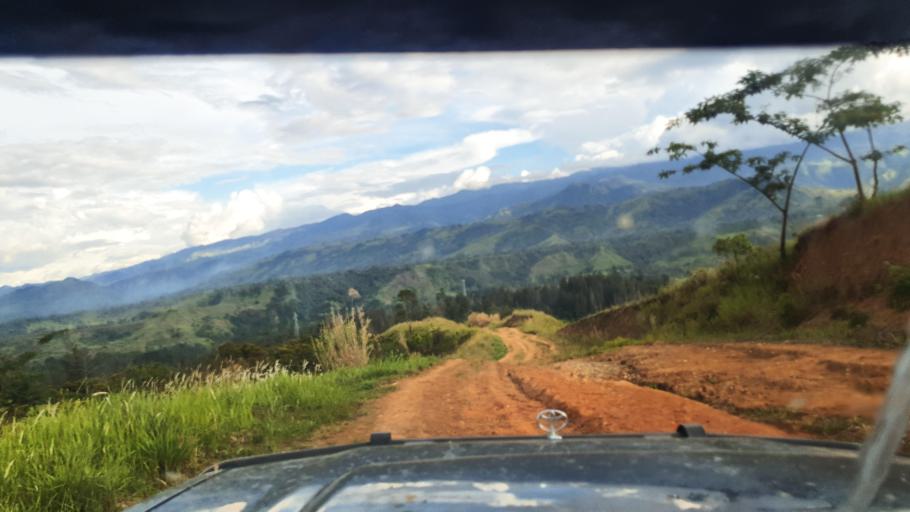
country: PG
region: Jiwaka
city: Minj
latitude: -5.9317
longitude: 144.8194
